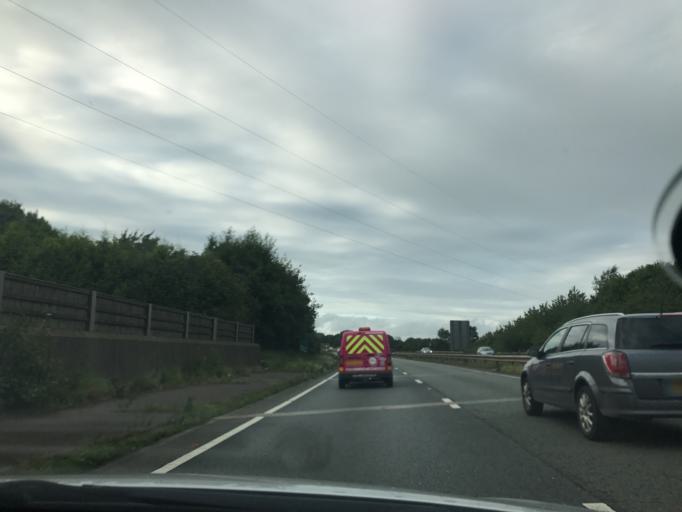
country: GB
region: England
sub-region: Cheshire West and Chester
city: Guilden Sutton
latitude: 53.2058
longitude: -2.8441
